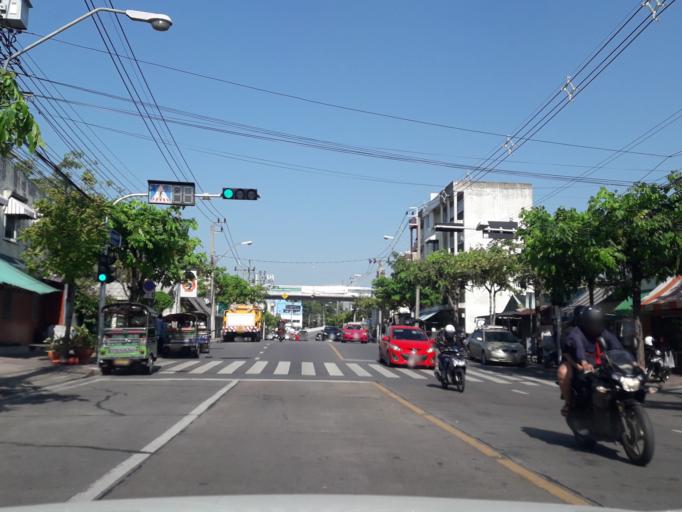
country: TH
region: Bangkok
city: Thon Buri
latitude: 13.7374
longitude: 100.4918
